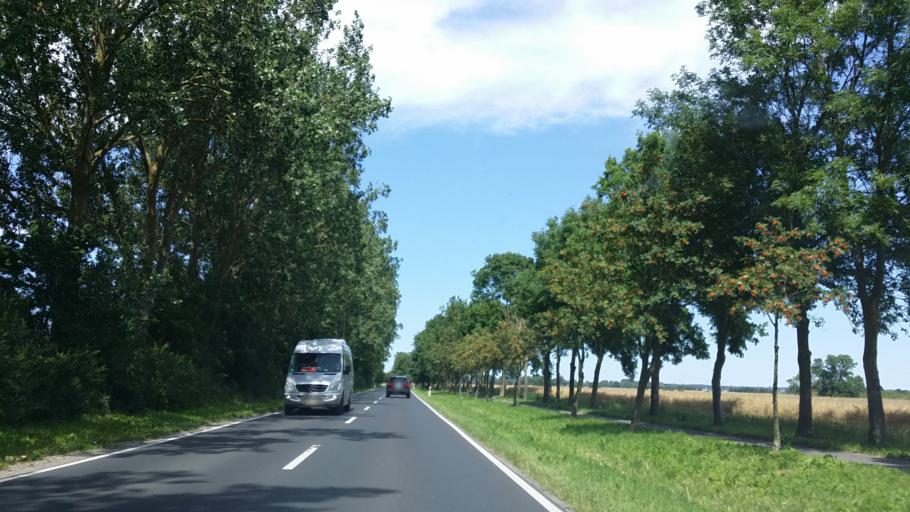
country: PL
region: West Pomeranian Voivodeship
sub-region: Powiat koszalinski
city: Mielno
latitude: 54.2248
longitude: 16.0761
